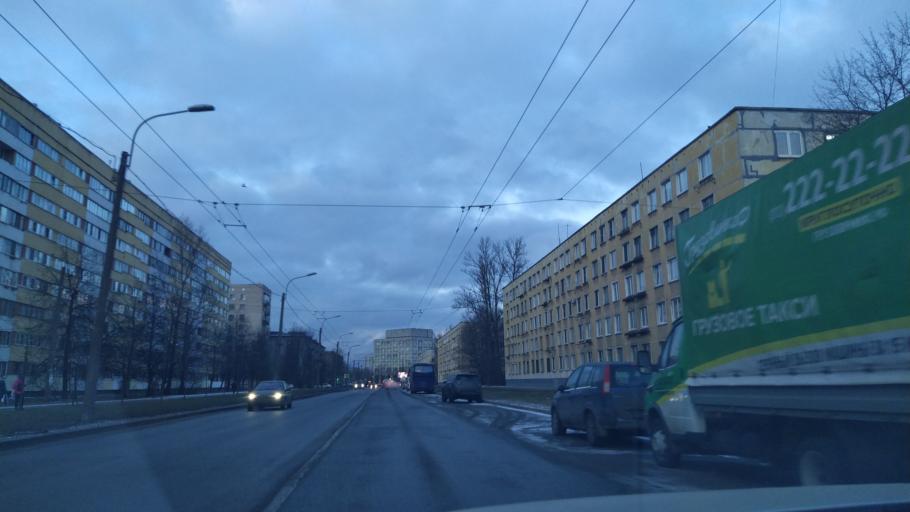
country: RU
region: St.-Petersburg
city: Dachnoye
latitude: 59.8534
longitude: 30.2563
